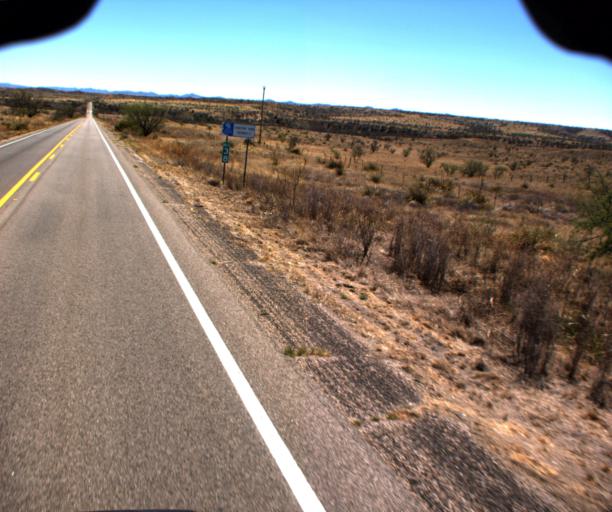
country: US
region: Arizona
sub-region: Pima County
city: Corona de Tucson
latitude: 31.7470
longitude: -110.6692
